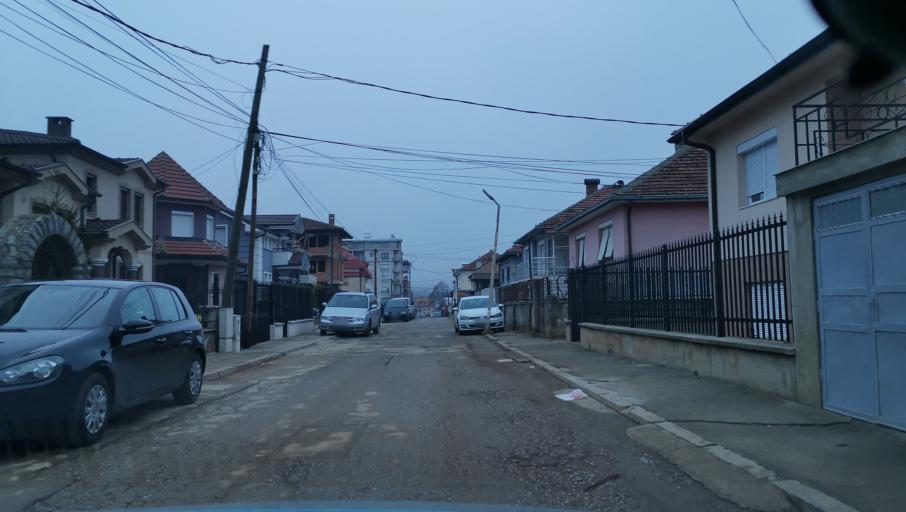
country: MK
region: Debar
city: Debar
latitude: 41.5156
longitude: 20.5273
